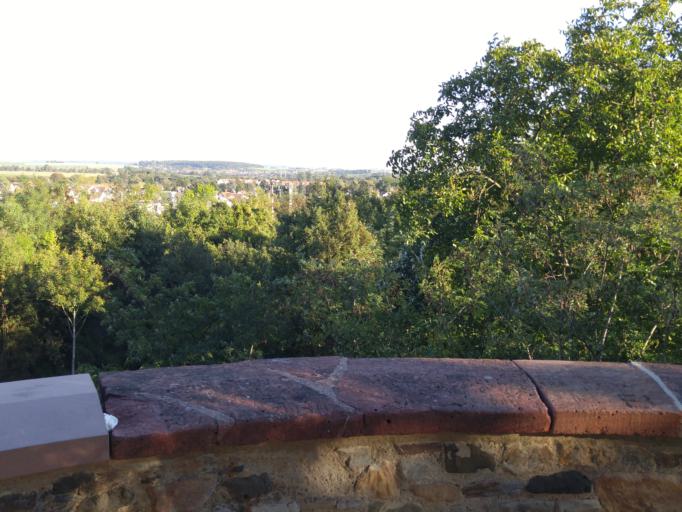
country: DE
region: Hesse
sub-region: Regierungsbezirk Darmstadt
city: Friedberg
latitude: 50.3408
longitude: 8.7558
